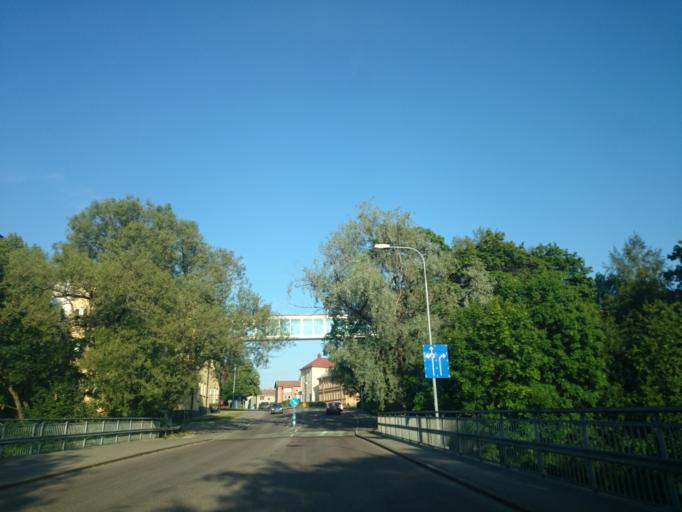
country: SE
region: Vaesternorrland
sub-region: Sundsvalls Kommun
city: Sundsvall
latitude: 62.3935
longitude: 17.2808
